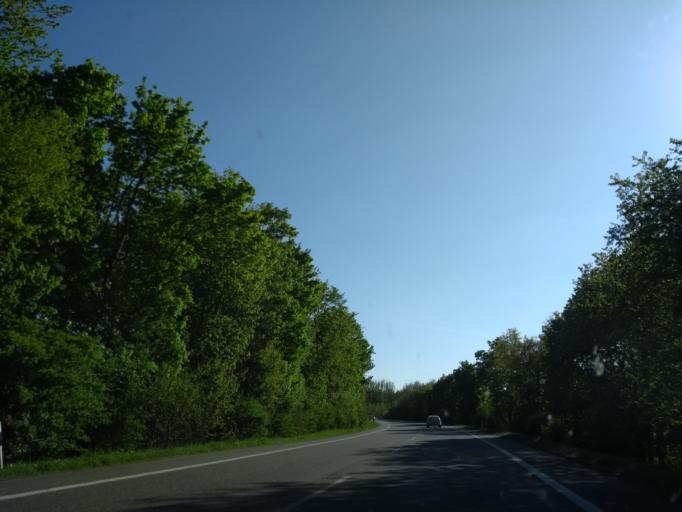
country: DE
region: Hesse
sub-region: Regierungsbezirk Giessen
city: Breidenbach
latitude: 50.9085
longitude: 8.4556
